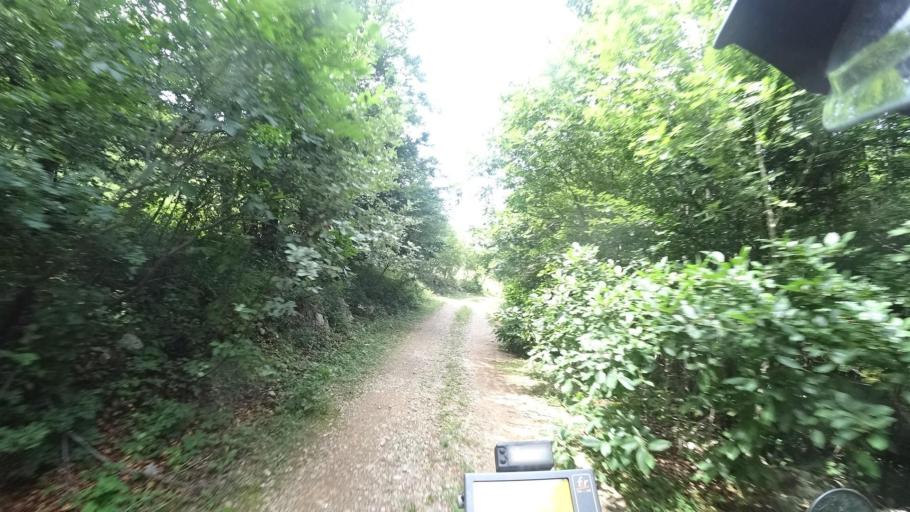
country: HR
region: Primorsko-Goranska
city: Novi Vinodolski
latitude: 45.1200
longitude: 14.9092
